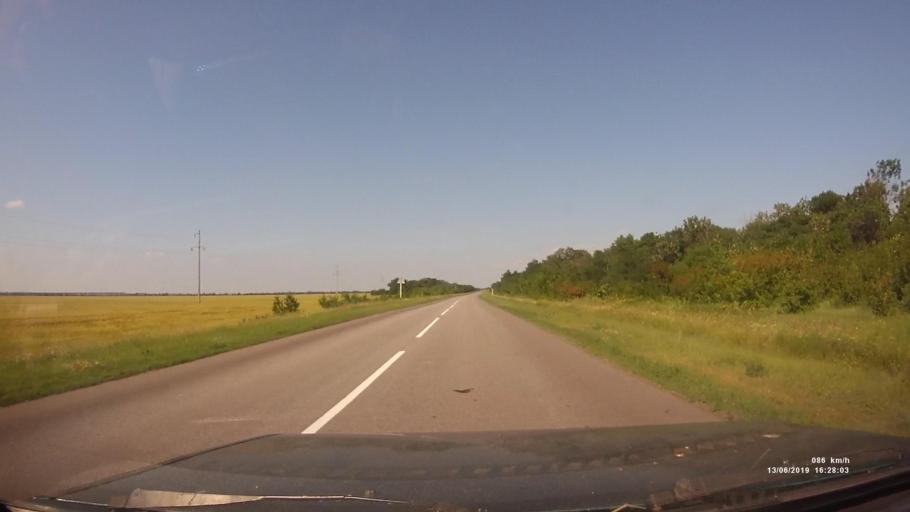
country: RU
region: Rostov
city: Kazanskaya
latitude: 49.8182
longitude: 41.1933
